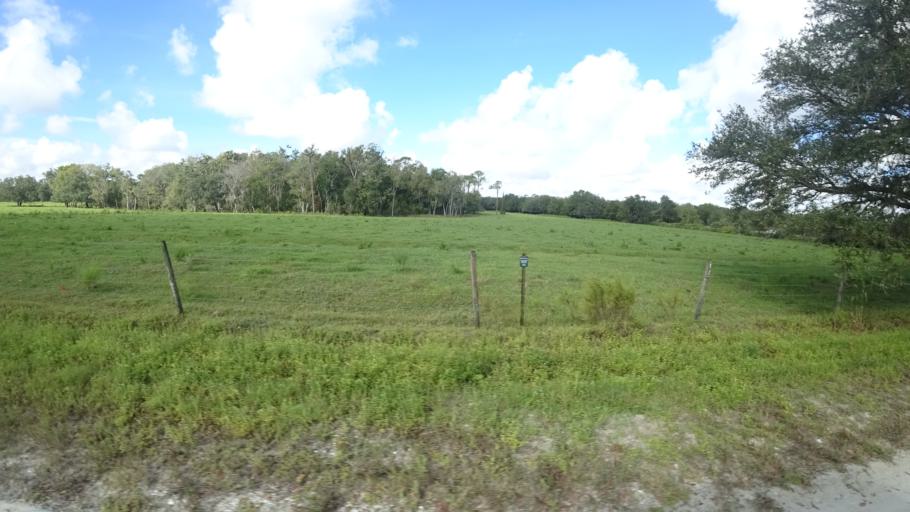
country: US
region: Florida
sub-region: Sarasota County
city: Lake Sarasota
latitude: 27.3348
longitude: -82.2039
